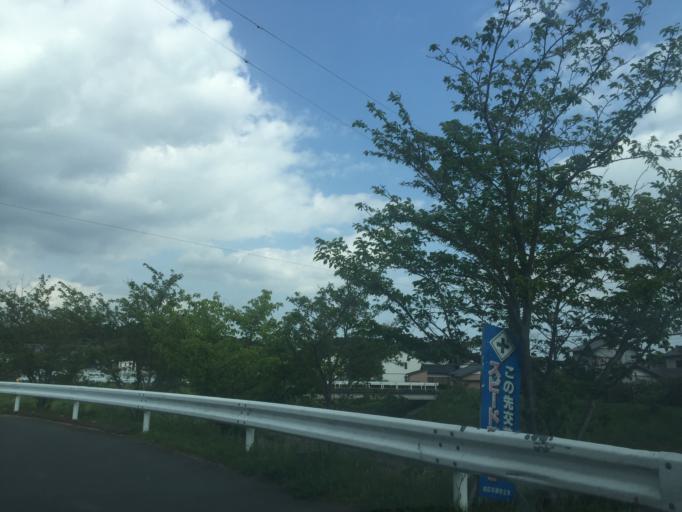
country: JP
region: Shizuoka
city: Kakegawa
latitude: 34.7824
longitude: 138.0097
